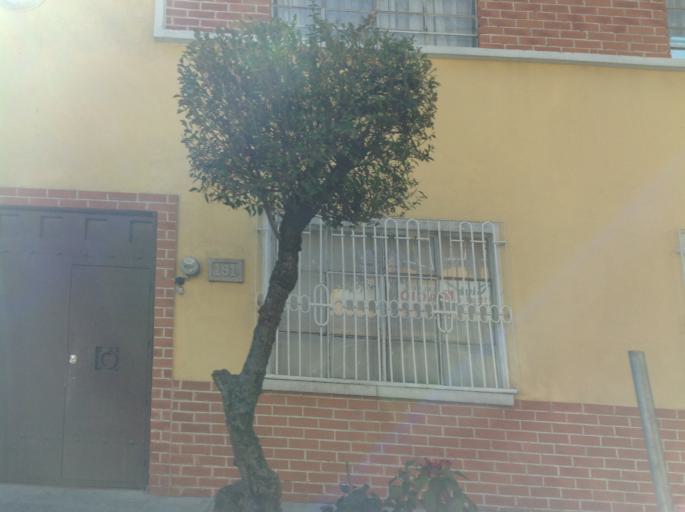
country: MX
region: Mexico City
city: Azcapotzalco
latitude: 19.4670
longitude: -99.1795
